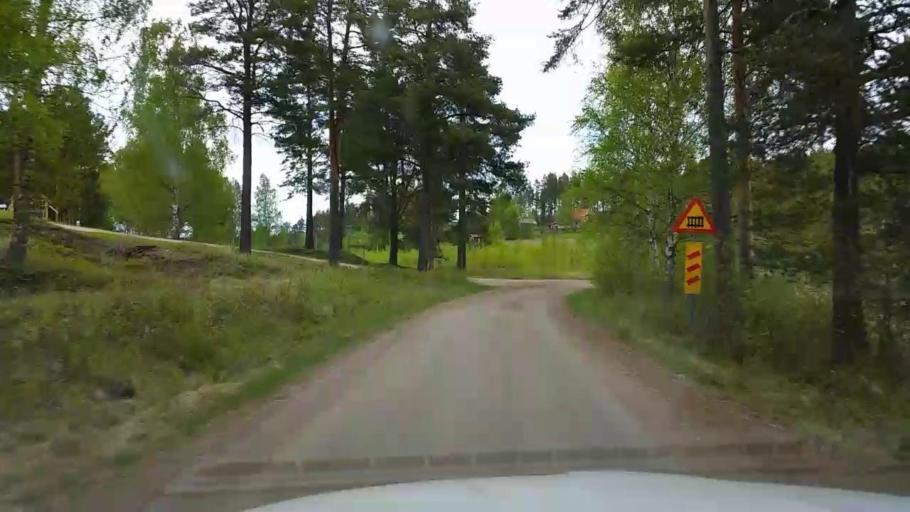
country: SE
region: Vaesternorrland
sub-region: Ange Kommun
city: Ange
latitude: 62.1531
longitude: 15.6745
